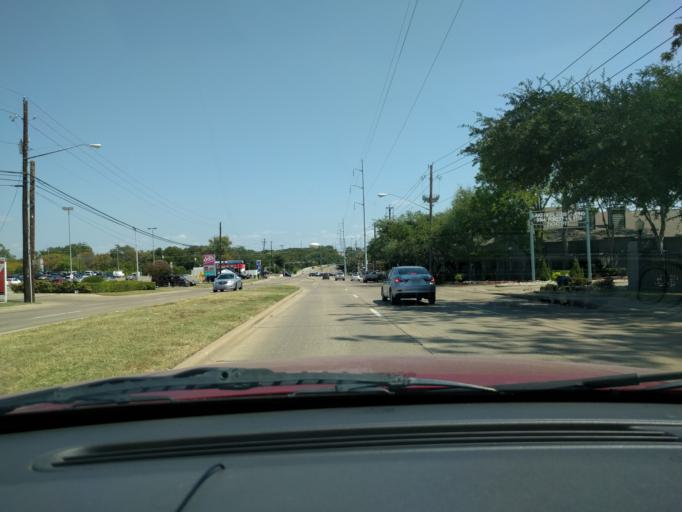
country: US
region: Texas
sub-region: Dallas County
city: Richardson
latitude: 32.9095
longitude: -96.7204
